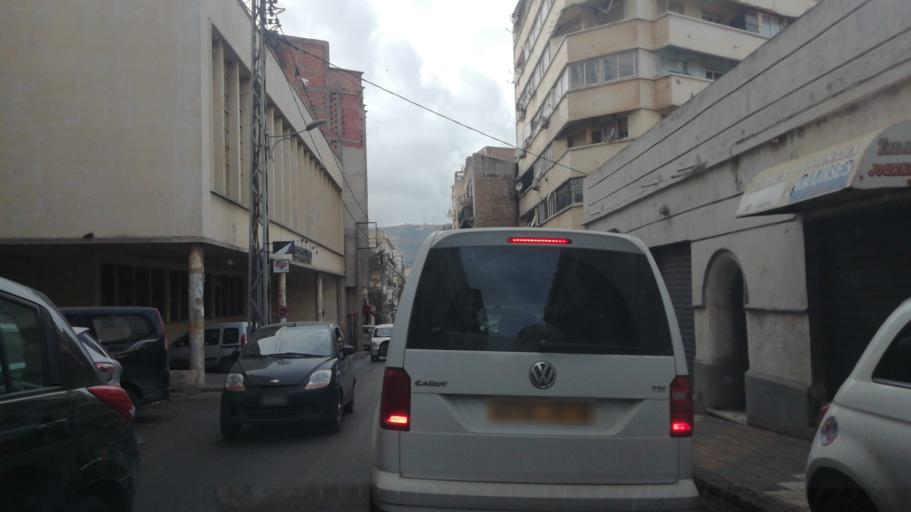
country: DZ
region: Oran
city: Oran
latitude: 35.7025
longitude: -0.6343
